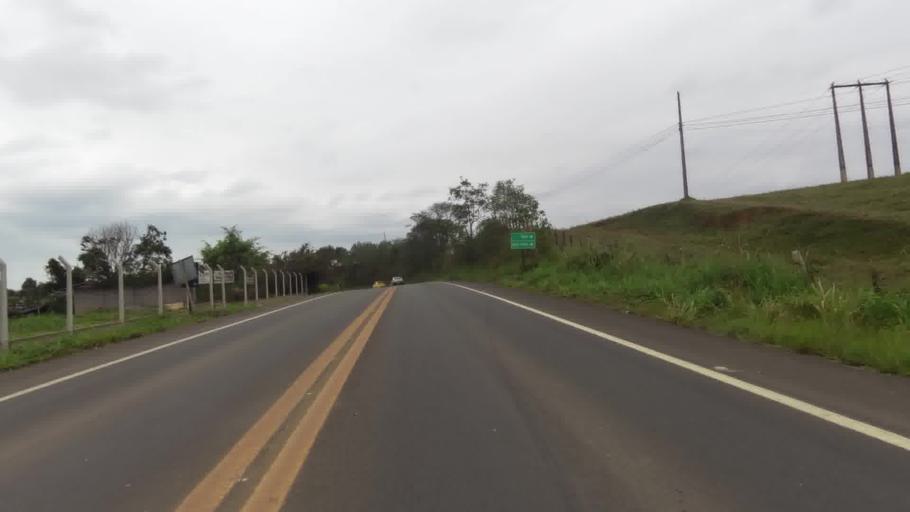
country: BR
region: Espirito Santo
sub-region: Piuma
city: Piuma
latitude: -20.8221
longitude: -40.6958
